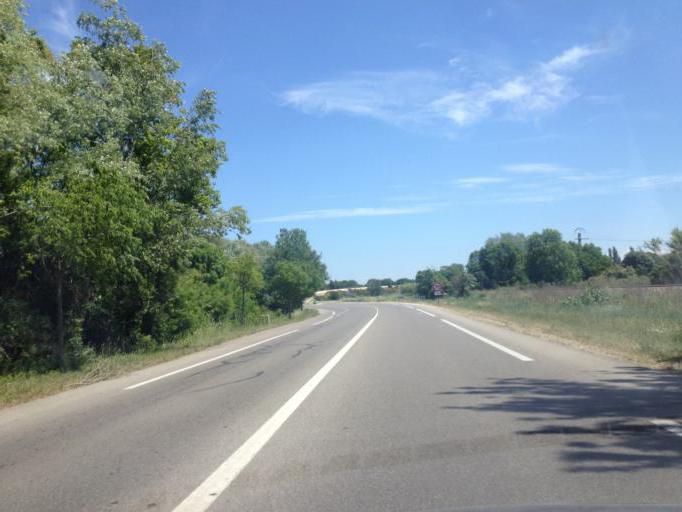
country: FR
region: Provence-Alpes-Cote d'Azur
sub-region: Departement du Vaucluse
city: Lauris
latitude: 43.7386
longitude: 5.3341
